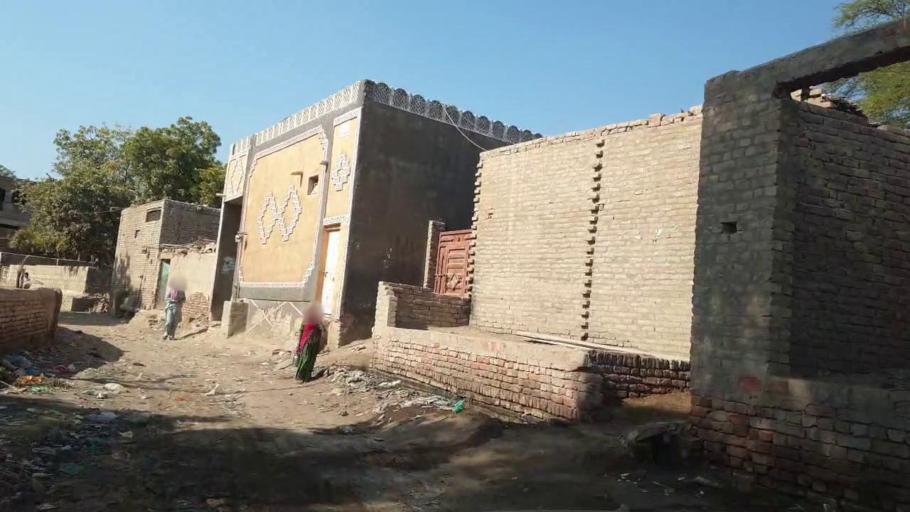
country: PK
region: Sindh
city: Tando Allahyar
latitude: 25.5716
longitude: 68.7144
